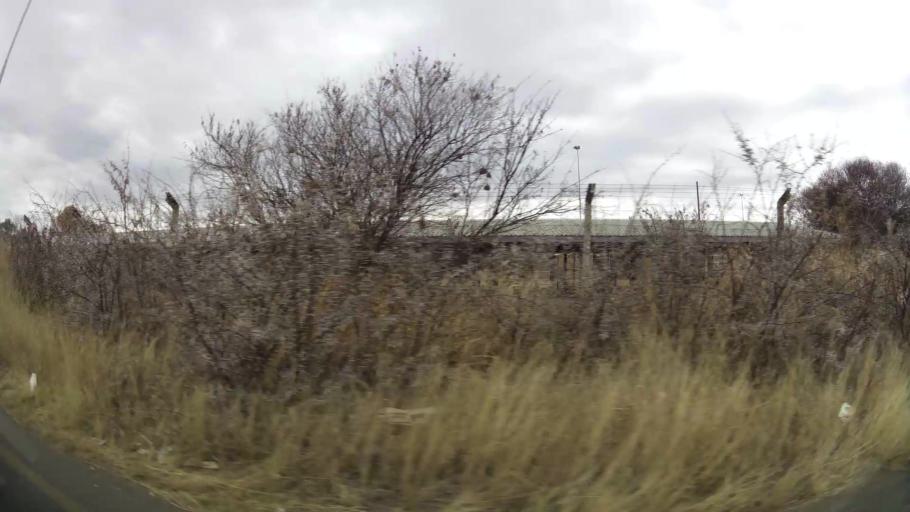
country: ZA
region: Orange Free State
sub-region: Fezile Dabi District Municipality
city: Kroonstad
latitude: -27.6536
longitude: 27.2266
